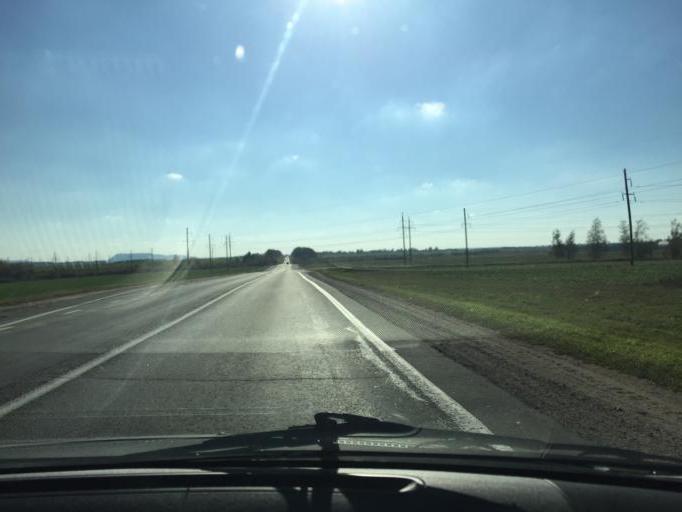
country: BY
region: Minsk
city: Slutsk
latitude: 52.9814
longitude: 27.5042
